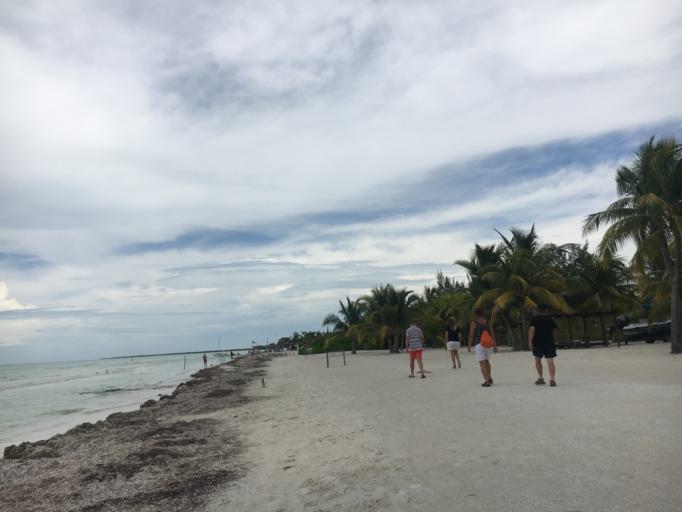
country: MX
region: Quintana Roo
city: Kantunilkin
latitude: 21.5263
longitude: -87.3782
